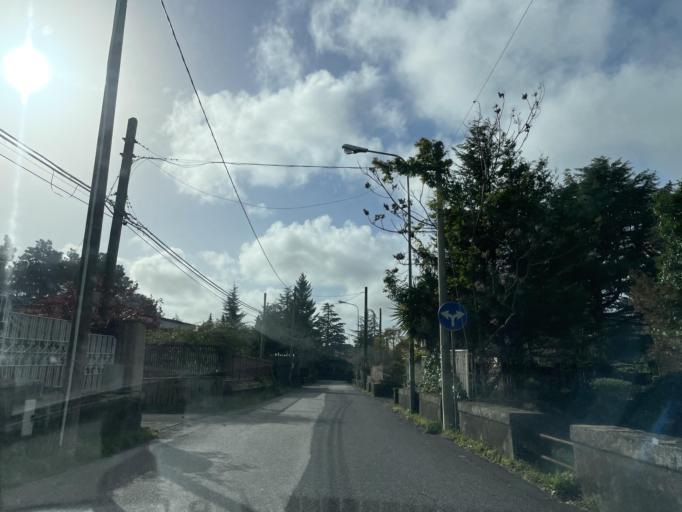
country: IT
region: Sicily
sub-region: Catania
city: Nicolosi
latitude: 37.6212
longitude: 15.0244
